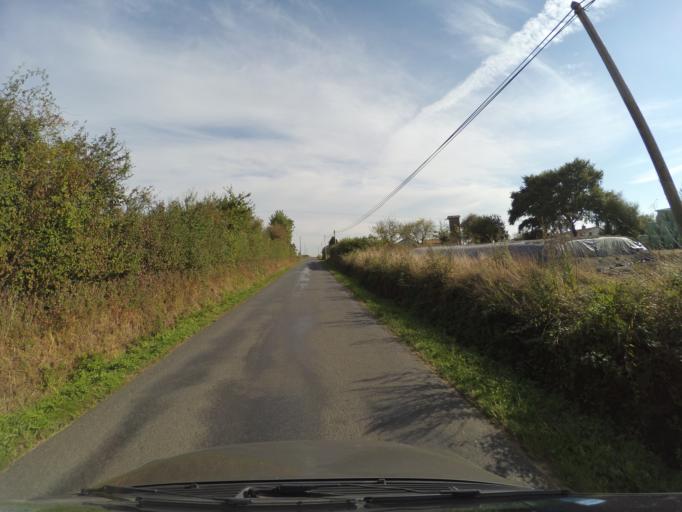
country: FR
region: Pays de la Loire
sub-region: Departement de Maine-et-Loire
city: Tillieres
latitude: 47.1326
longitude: -1.1909
